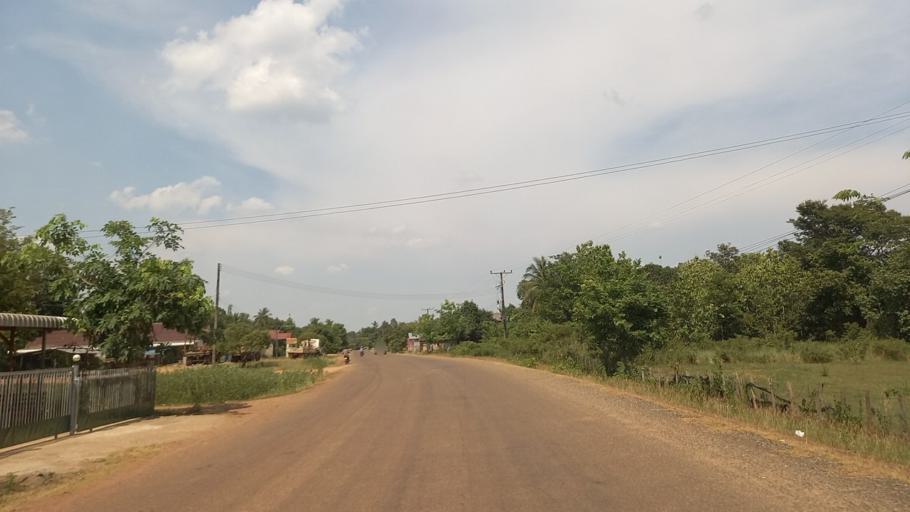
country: LA
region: Bolikhamxai
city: Muang Pakxan
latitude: 18.4046
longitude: 103.6949
